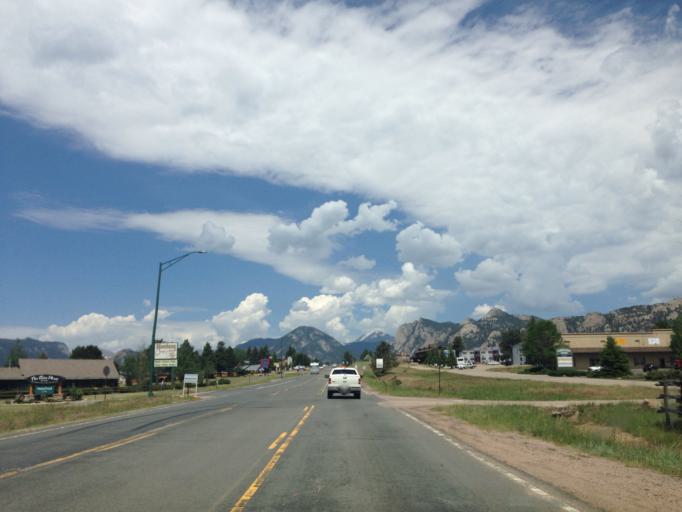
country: US
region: Colorado
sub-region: Larimer County
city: Estes Park
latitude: 40.3798
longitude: -105.4915
